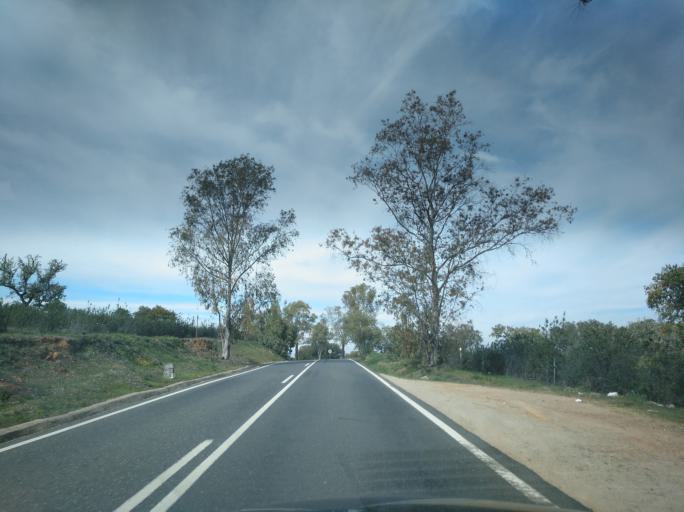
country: PT
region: Beja
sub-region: Mertola
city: Mertola
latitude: 37.7157
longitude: -7.7557
